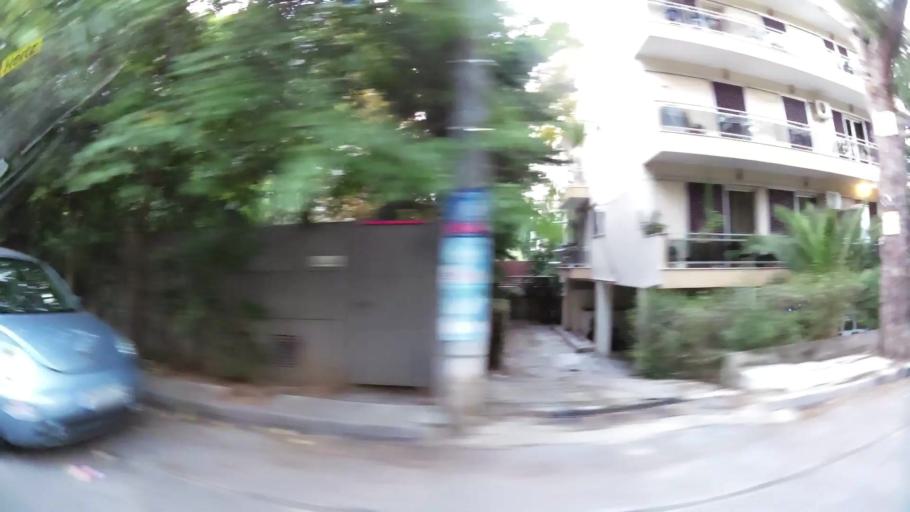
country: GR
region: Attica
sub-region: Nomarchia Athinas
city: Filothei
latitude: 38.0270
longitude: 23.7863
